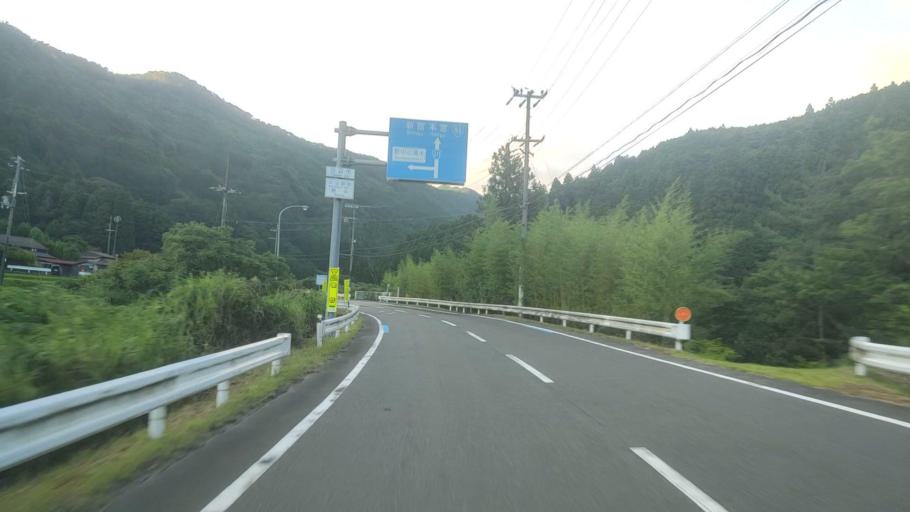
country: JP
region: Wakayama
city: Tanabe
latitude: 33.8225
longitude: 135.6310
